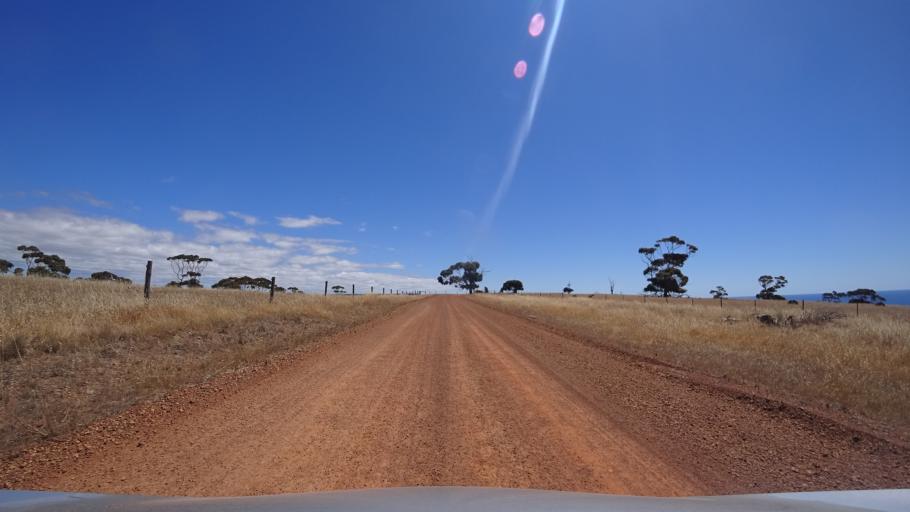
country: AU
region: South Australia
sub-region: Kangaroo Island
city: Kingscote
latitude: -35.6787
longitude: 136.9874
